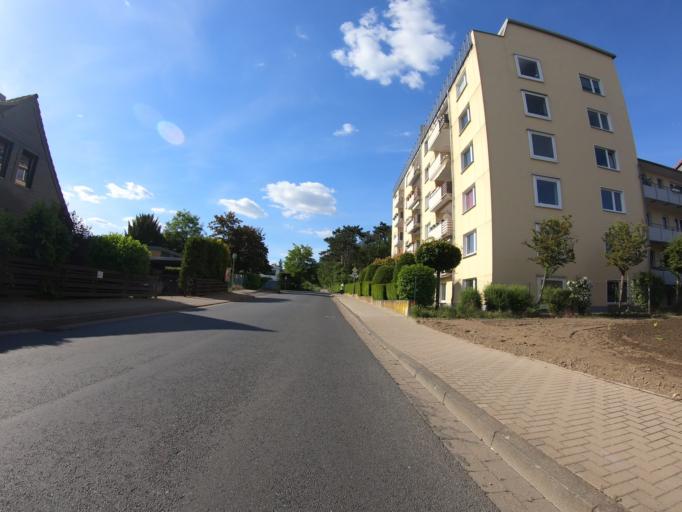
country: DE
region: Lower Saxony
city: Wolfenbuettel
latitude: 52.1807
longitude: 10.5310
